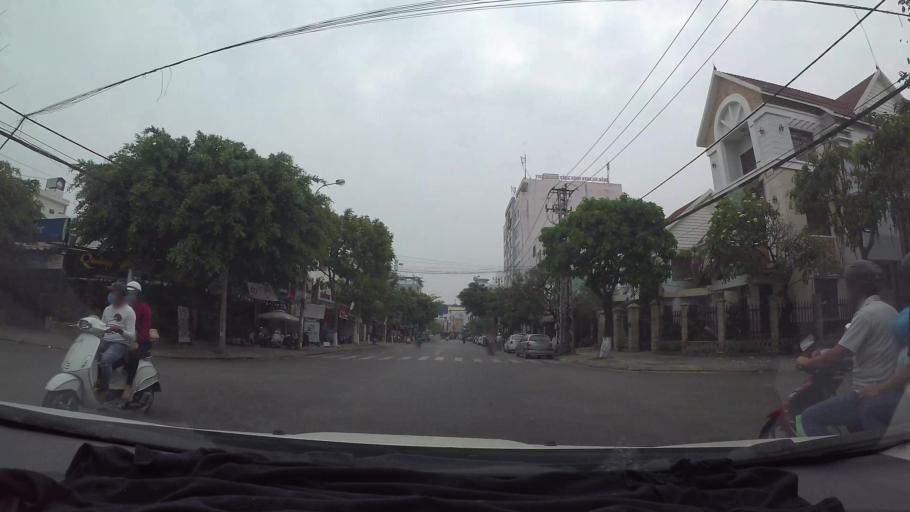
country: VN
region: Da Nang
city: Cam Le
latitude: 16.0361
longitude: 108.2155
